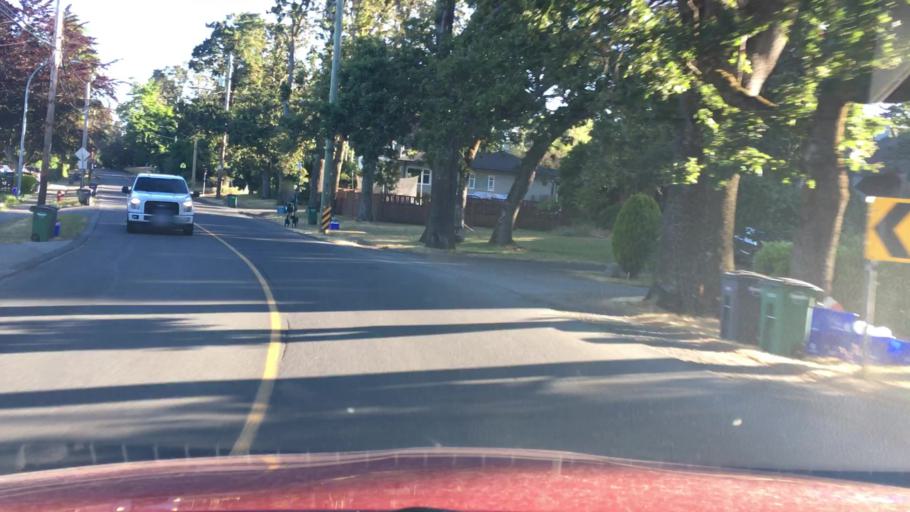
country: CA
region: British Columbia
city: Oak Bay
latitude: 48.4491
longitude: -123.3253
